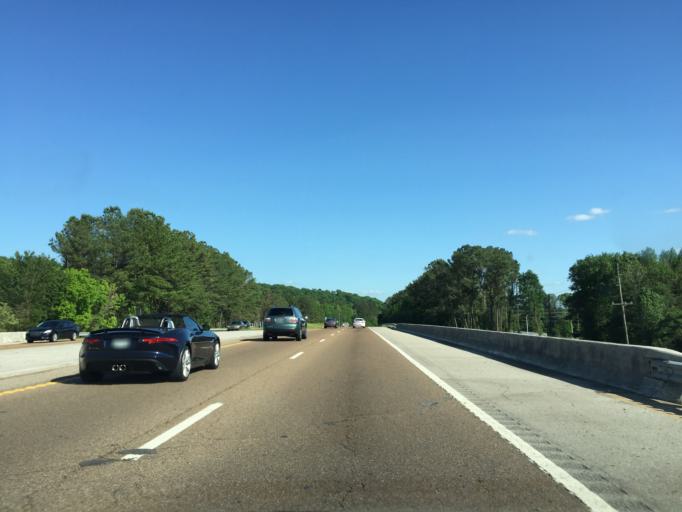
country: US
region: Tennessee
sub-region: Hamilton County
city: East Chattanooga
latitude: 35.1177
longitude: -85.2344
